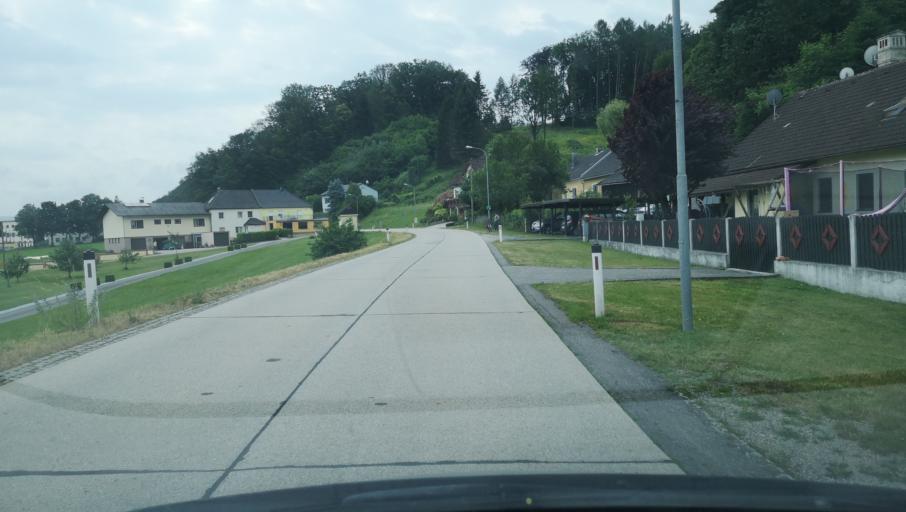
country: AT
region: Lower Austria
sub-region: Politischer Bezirk Melk
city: Ybbs an der Donau
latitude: 48.1909
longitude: 15.0605
